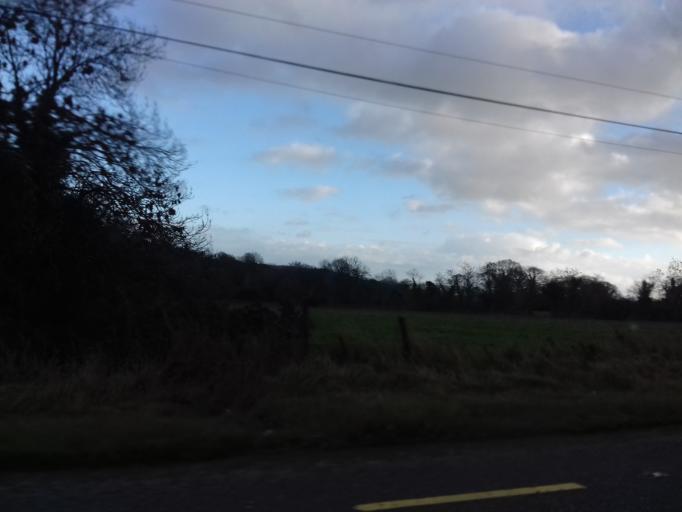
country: IE
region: Leinster
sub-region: An Mhi
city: Slane
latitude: 53.7576
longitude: -6.4972
